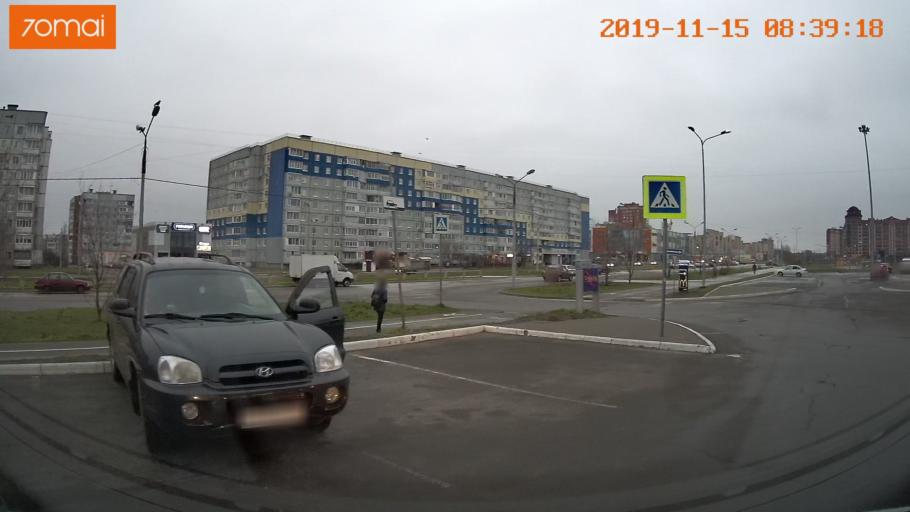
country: RU
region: Vologda
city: Cherepovets
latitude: 59.0927
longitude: 37.9176
